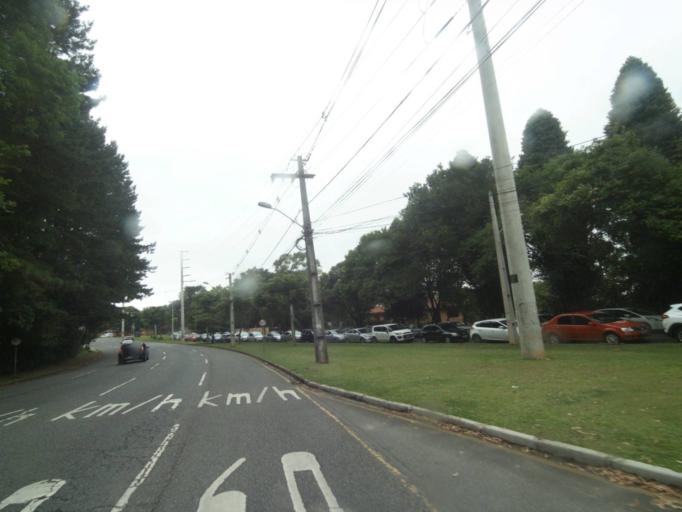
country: BR
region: Parana
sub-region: Curitiba
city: Curitiba
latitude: -25.4424
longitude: -49.3374
